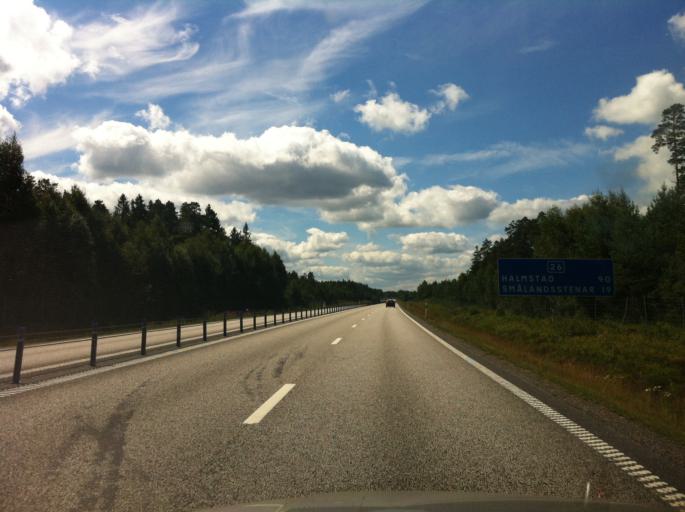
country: SE
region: Joenkoeping
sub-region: Gislaveds Kommun
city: Gislaved
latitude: 57.3279
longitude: 13.5463
